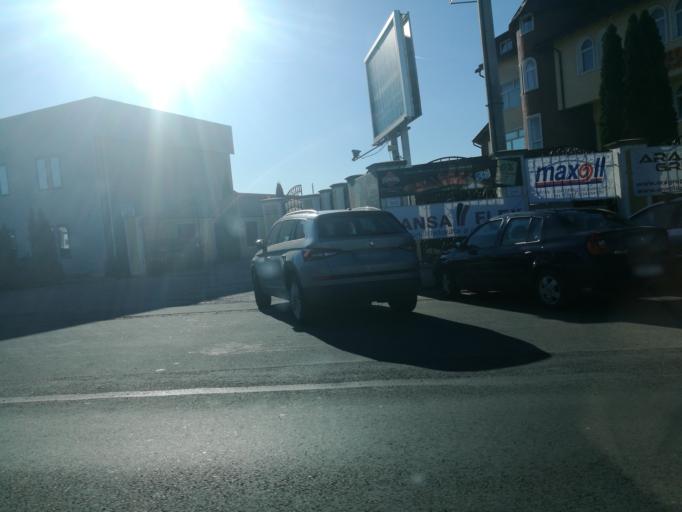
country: RO
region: Brasov
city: Brasov
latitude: 45.6723
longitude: 25.5900
